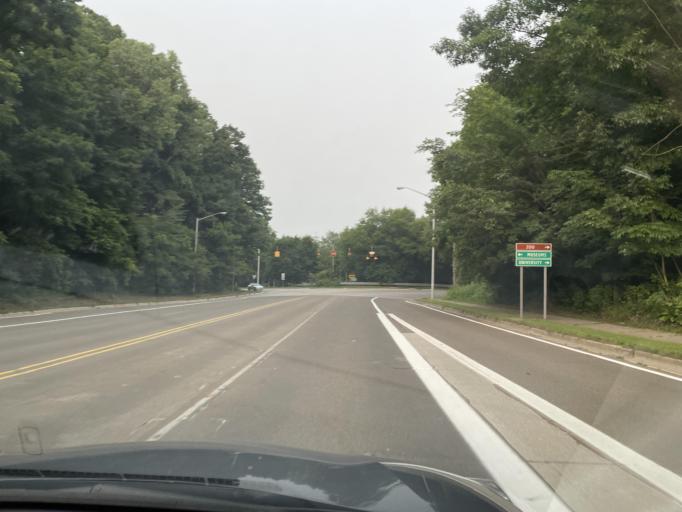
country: US
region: Michigan
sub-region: Kent County
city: Grand Rapids
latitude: 42.9656
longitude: -85.7034
